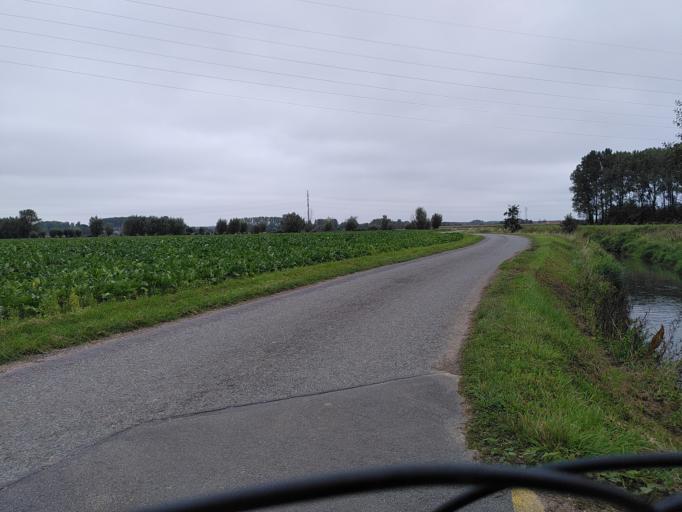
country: FR
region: Nord-Pas-de-Calais
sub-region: Departement du Pas-de-Calais
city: Guarbecque
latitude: 50.6220
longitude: 2.4889
